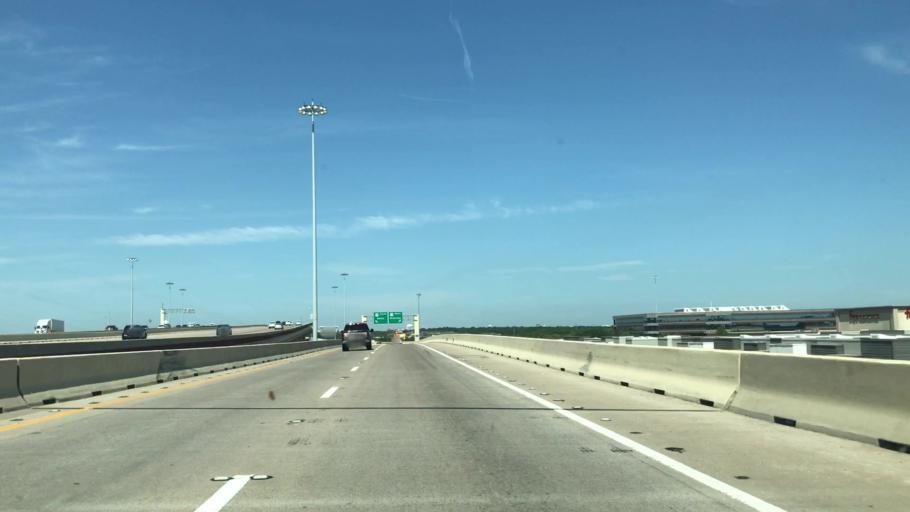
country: US
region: Texas
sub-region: Collin County
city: Plano
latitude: 33.0041
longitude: -96.7019
